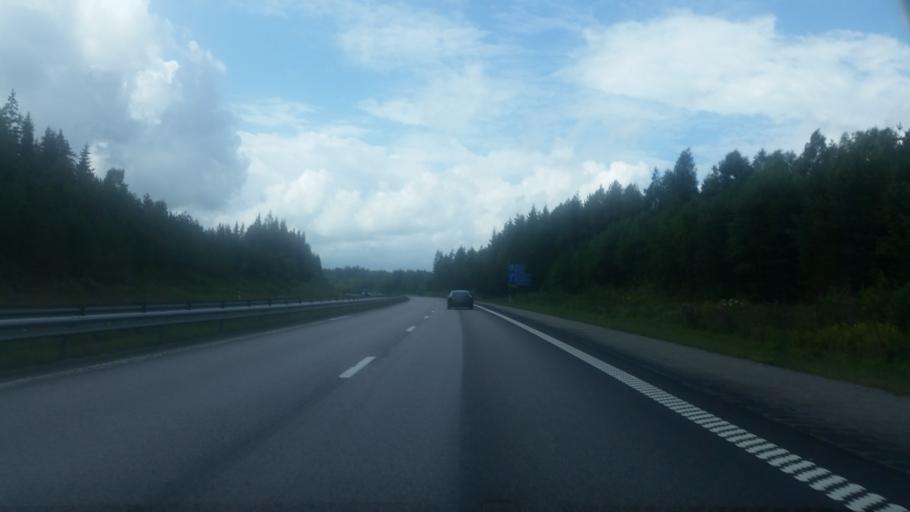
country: SE
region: Vaestra Goetaland
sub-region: Bollebygds Kommun
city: Bollebygd
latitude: 57.6711
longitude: 12.6302
